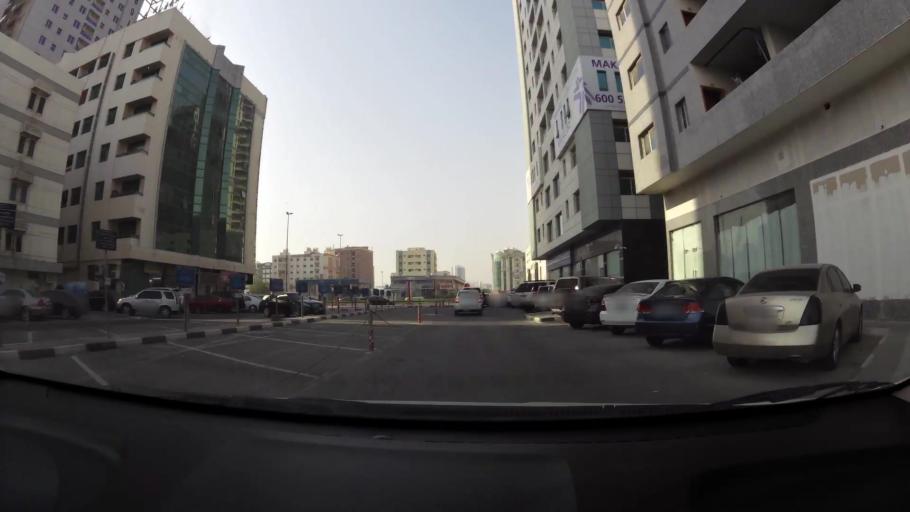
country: AE
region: Ajman
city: Ajman
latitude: 25.3913
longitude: 55.4380
